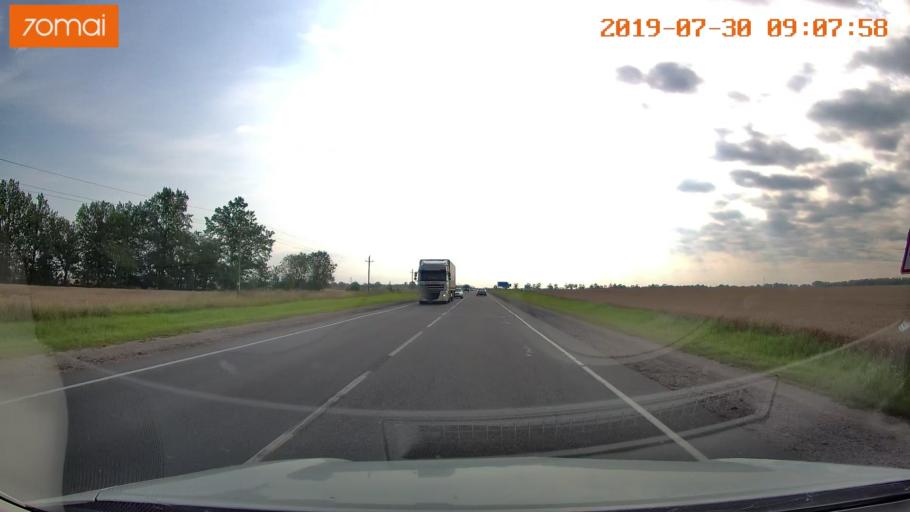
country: RU
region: Kaliningrad
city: Gusev
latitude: 54.6121
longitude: 22.3746
